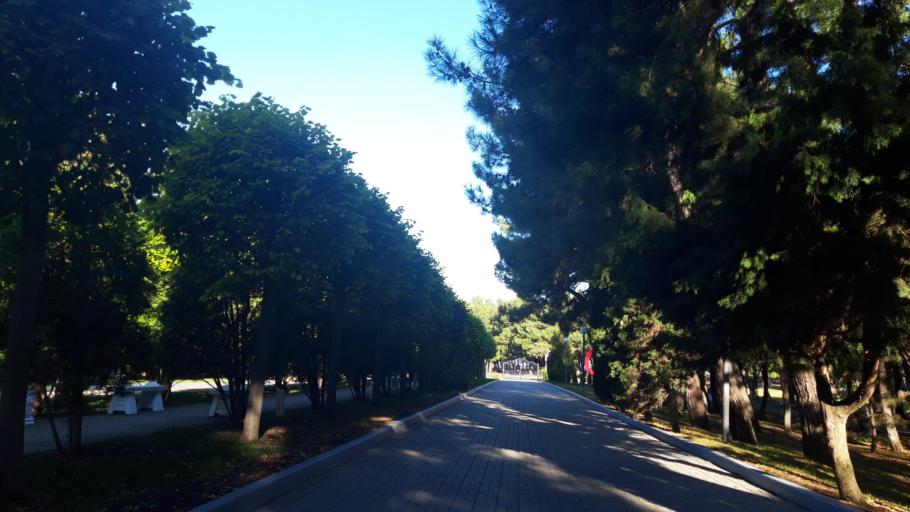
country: RU
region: Krasnodarskiy
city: Gelendzhik
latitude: 44.5522
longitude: 38.0535
